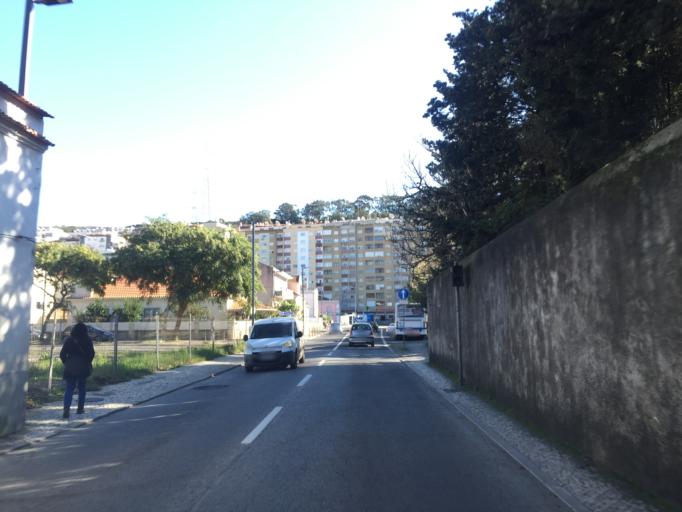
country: PT
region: Lisbon
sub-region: Sintra
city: Belas
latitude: 38.7755
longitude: -9.2623
